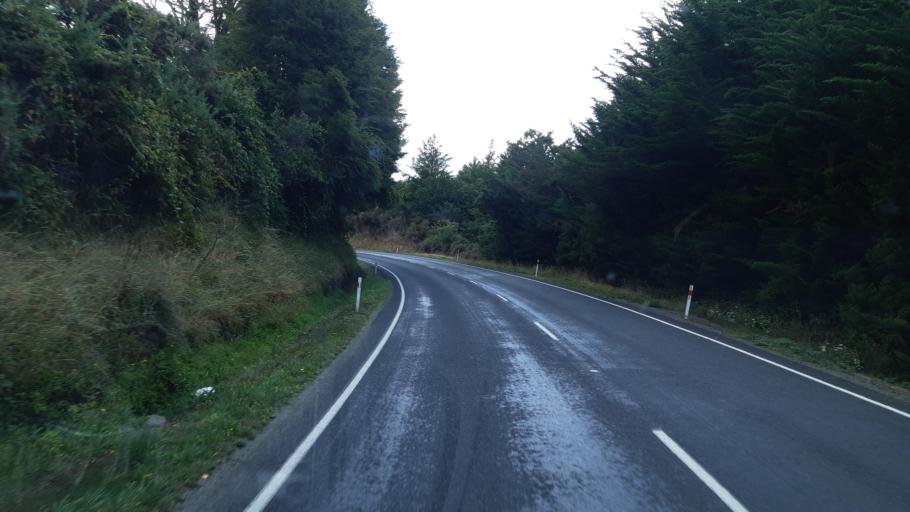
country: NZ
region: Tasman
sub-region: Tasman District
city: Wakefield
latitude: -41.5546
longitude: 172.7877
